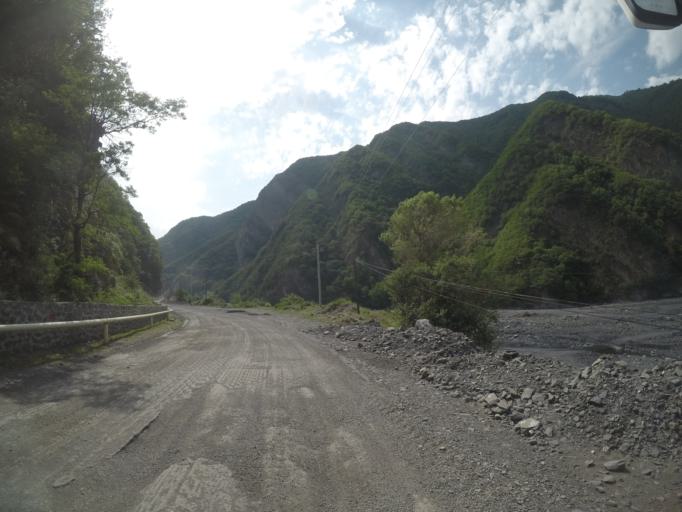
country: AZ
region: Qakh Rayon
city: Qaxbas
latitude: 41.4641
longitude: 47.0363
